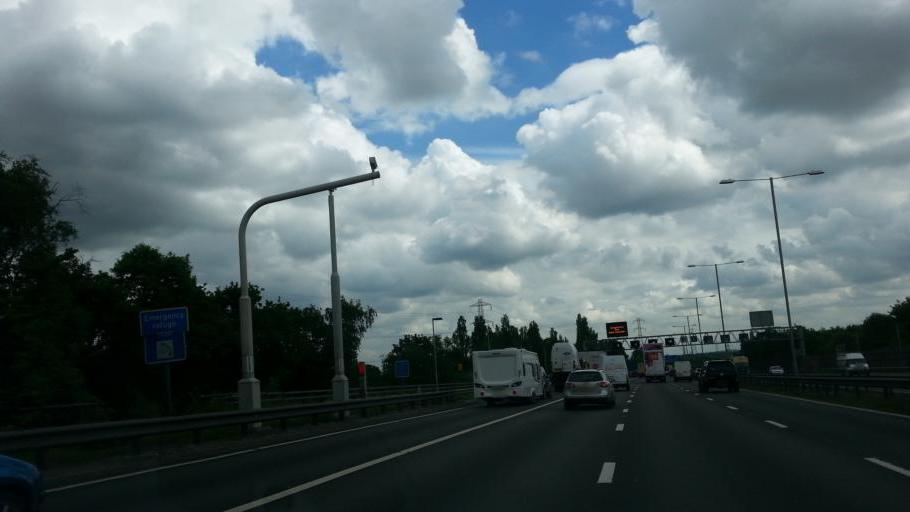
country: GB
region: England
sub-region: Walsall
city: Bloxwich
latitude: 52.6094
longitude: -2.0227
